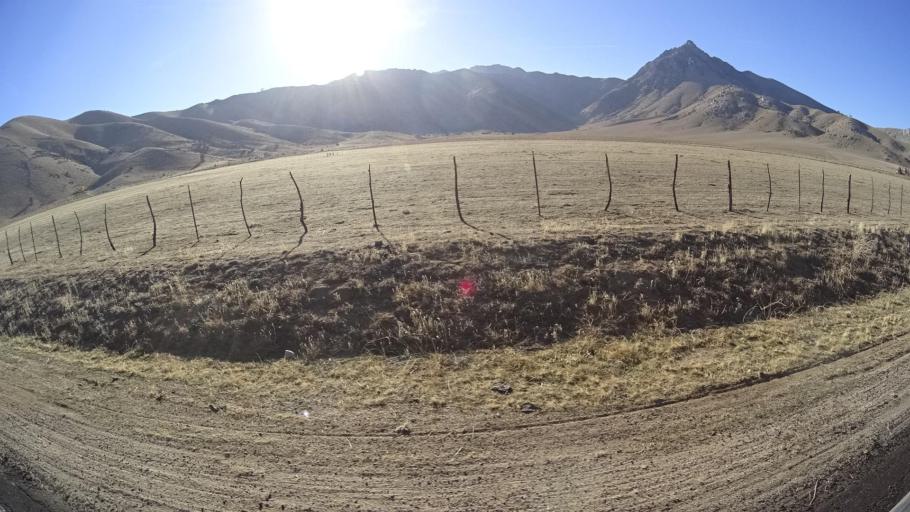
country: US
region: California
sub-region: Kern County
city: Weldon
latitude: 35.6208
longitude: -118.2557
